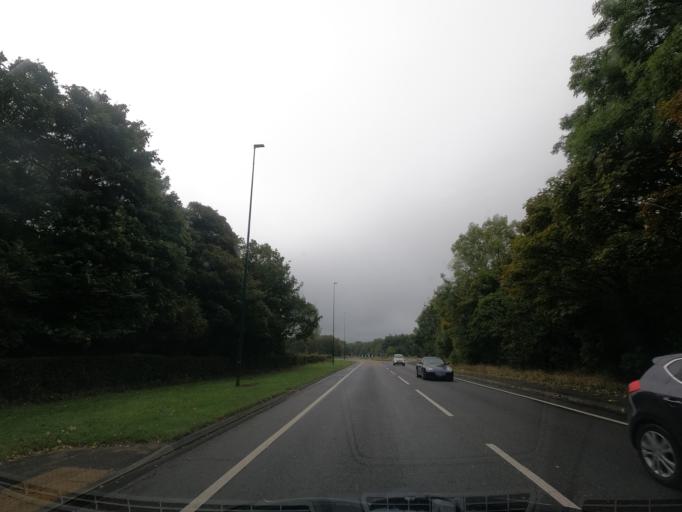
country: GB
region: England
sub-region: Redcar and Cleveland
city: Redcar
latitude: 54.5901
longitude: -1.0856
